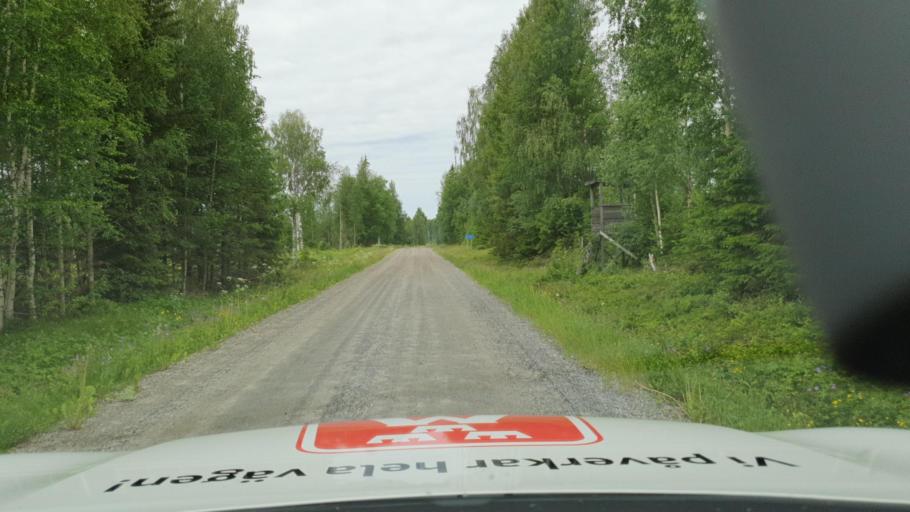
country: SE
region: Vaesterbotten
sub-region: Skelleftea Kommun
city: Burtraesk
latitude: 64.4467
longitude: 20.3400
